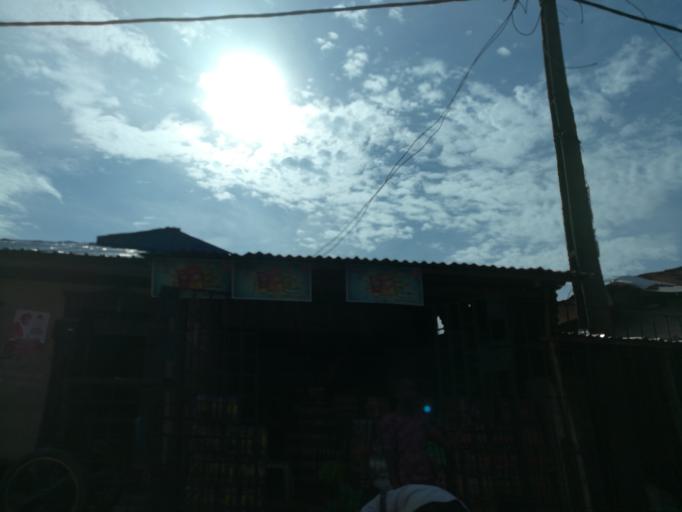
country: NG
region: Lagos
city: Oshodi
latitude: 6.5613
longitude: 3.3478
